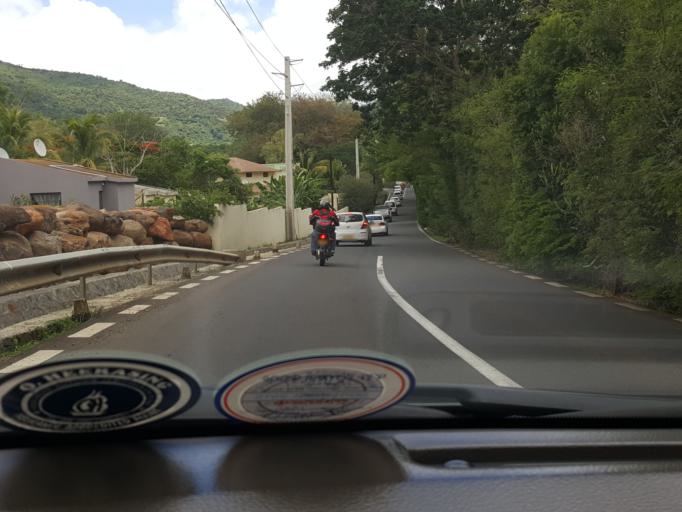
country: MU
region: Black River
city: Petite Case Noyale
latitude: -20.3875
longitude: 57.3819
